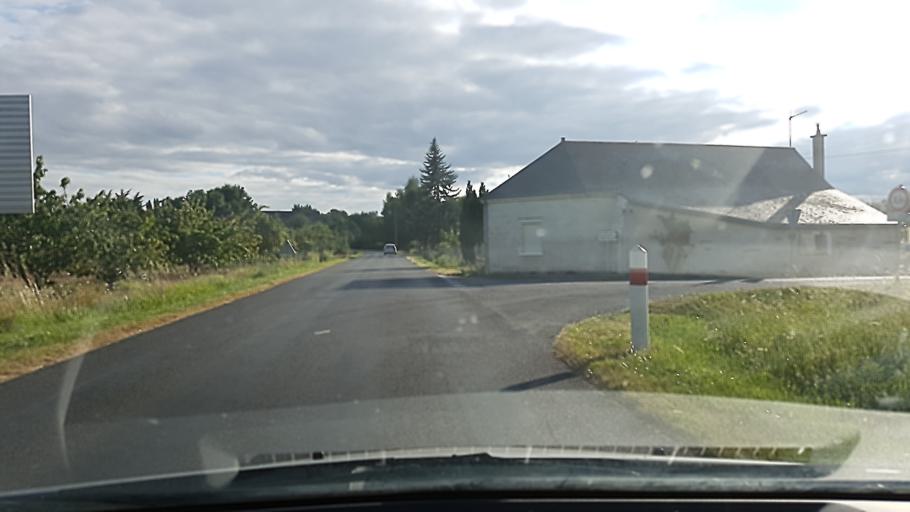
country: FR
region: Pays de la Loire
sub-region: Departement de Maine-et-Loire
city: Maze
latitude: 47.4529
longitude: -0.2786
